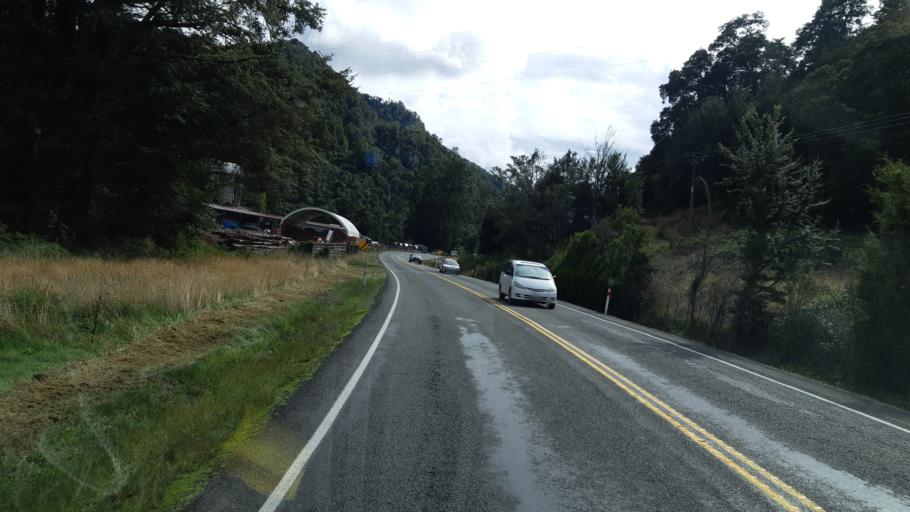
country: NZ
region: West Coast
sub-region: Buller District
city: Westport
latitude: -41.7936
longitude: 172.3653
